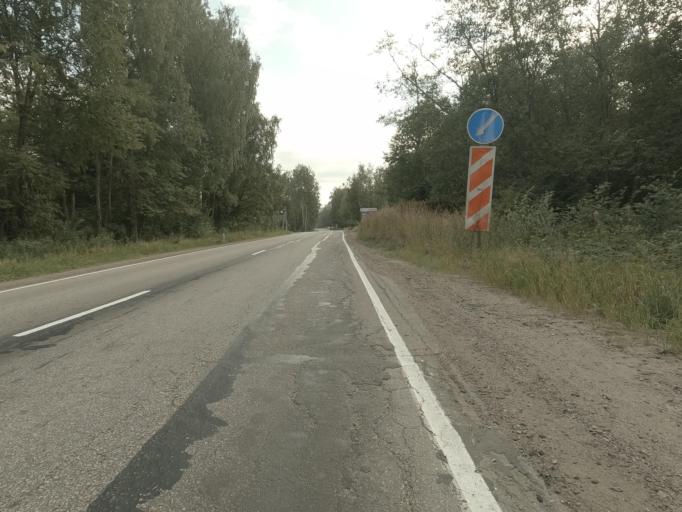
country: RU
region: Leningrad
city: Kamennogorsk
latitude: 60.8638
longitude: 28.9729
